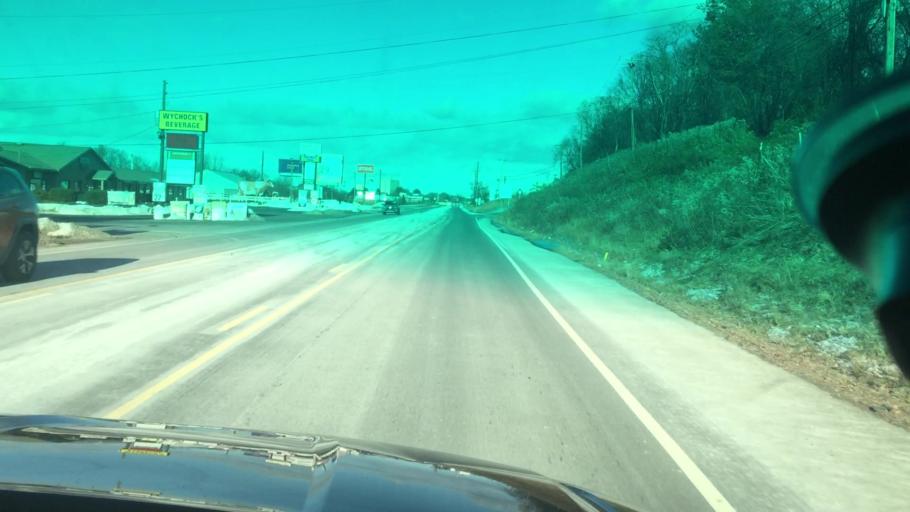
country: US
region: Pennsylvania
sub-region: Luzerne County
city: Georgetown
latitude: 41.2273
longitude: -75.8750
